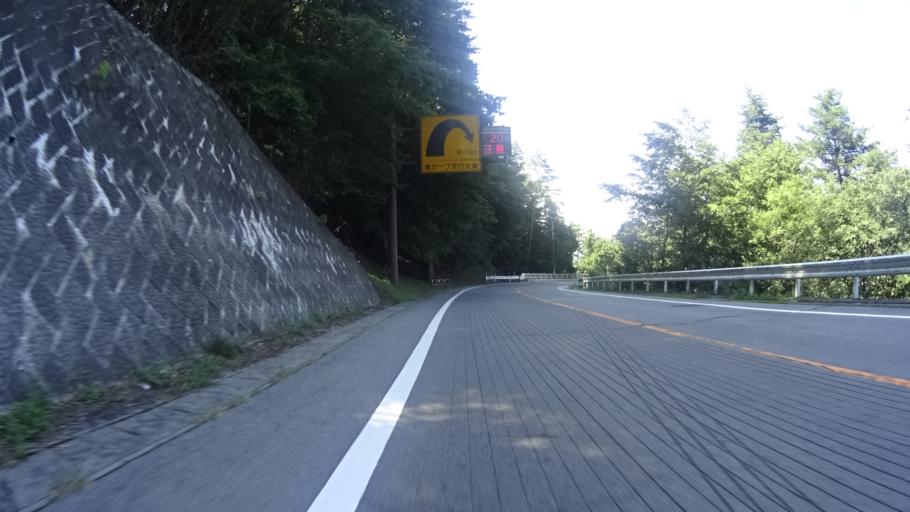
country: JP
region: Yamanashi
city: Enzan
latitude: 35.7509
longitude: 138.8102
